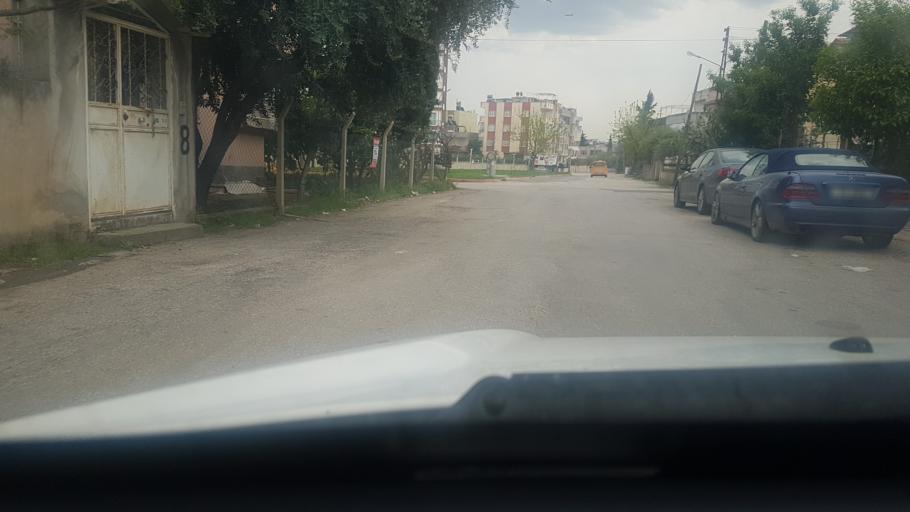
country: TR
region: Adana
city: Seyhan
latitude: 37.0204
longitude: 35.2761
